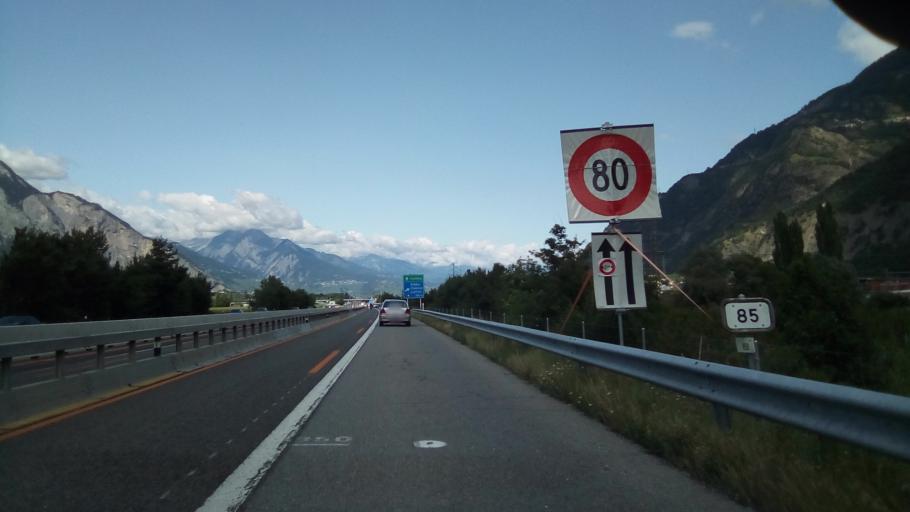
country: CH
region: Valais
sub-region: Martigny District
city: Saillon
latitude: 46.1647
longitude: 7.2024
